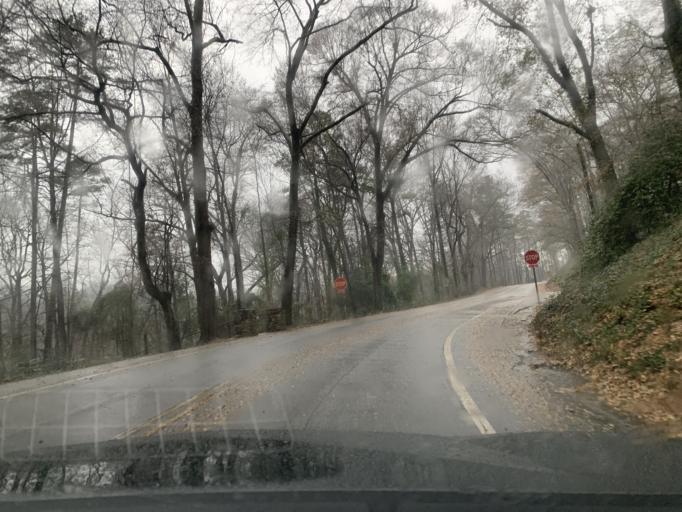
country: US
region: South Carolina
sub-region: Greenville County
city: Greenville
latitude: 34.8429
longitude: -82.3857
